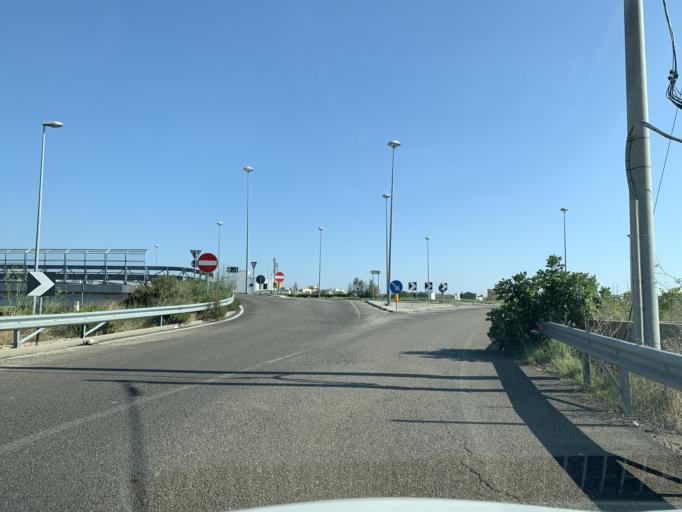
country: IT
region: Apulia
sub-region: Provincia di Lecce
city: Nardo
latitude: 40.1890
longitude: 18.0270
